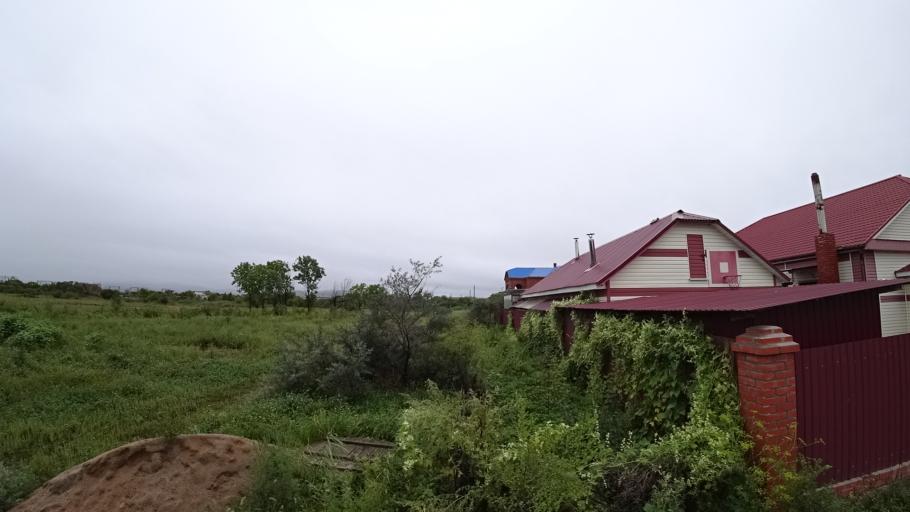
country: RU
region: Primorskiy
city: Monastyrishche
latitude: 44.2038
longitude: 132.4317
